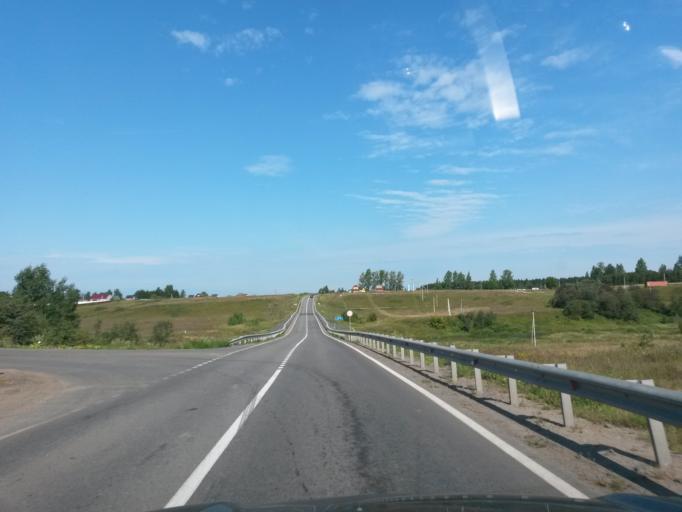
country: RU
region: Jaroslavl
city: Yaroslavl
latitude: 57.7856
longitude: 39.8383
